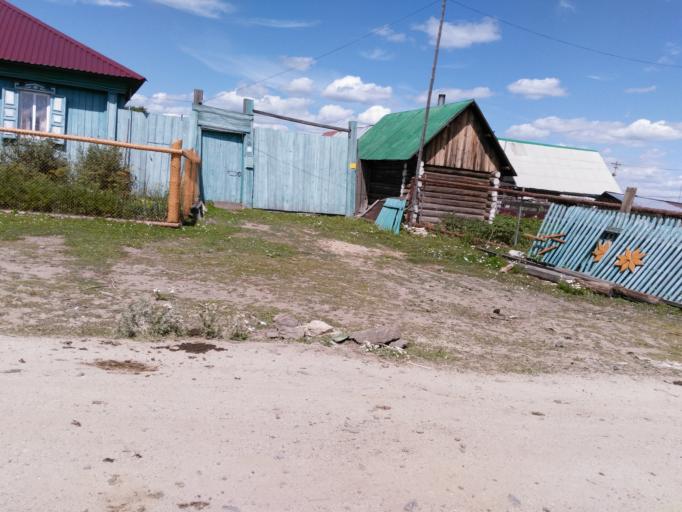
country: RU
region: Bashkortostan
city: Akhunovo
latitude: 54.2043
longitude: 59.6003
